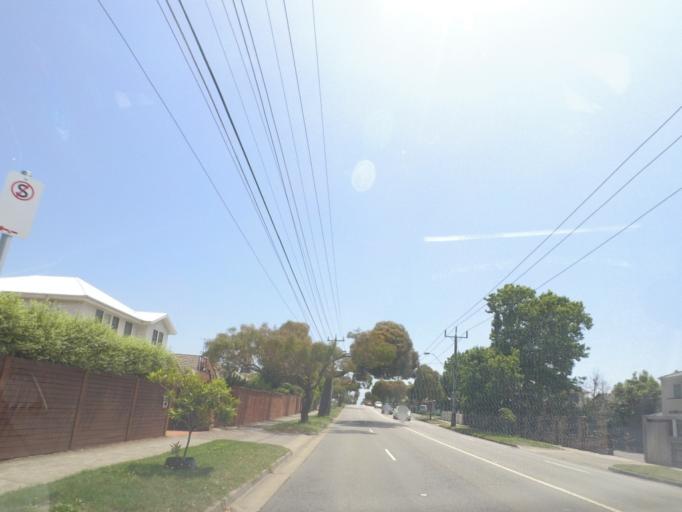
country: AU
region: Victoria
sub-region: Bayside
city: Hampton East
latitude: -37.9402
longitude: 145.0232
